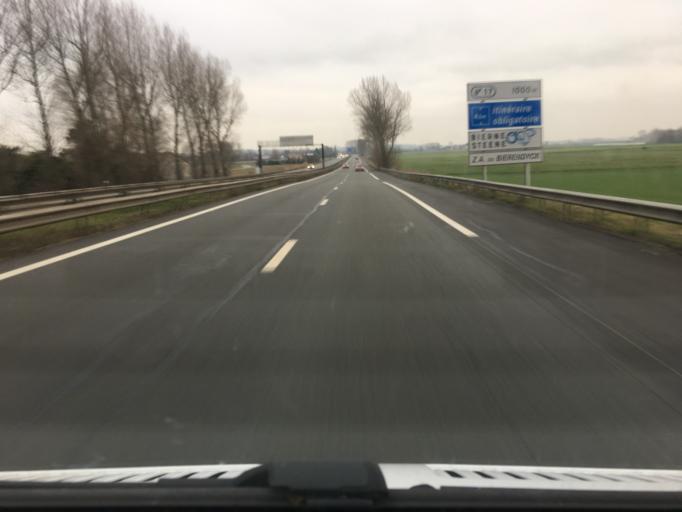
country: FR
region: Nord-Pas-de-Calais
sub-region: Departement du Nord
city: Bierne
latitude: 50.9689
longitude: 2.3965
